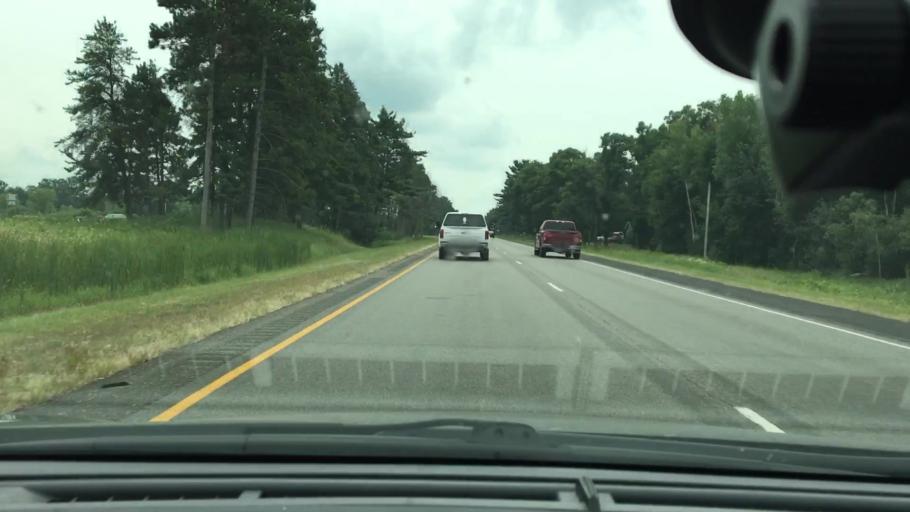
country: US
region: Minnesota
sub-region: Sherburne County
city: Zimmerman
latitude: 45.4823
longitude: -93.5828
